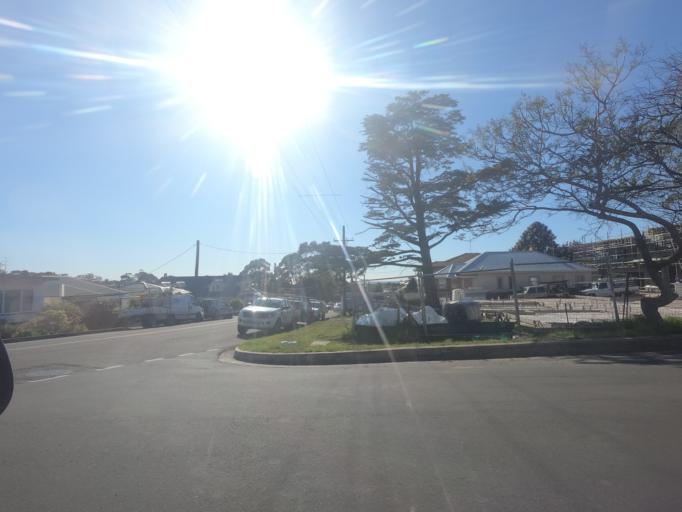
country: AU
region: New South Wales
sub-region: Wollongong
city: Corrimal
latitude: -34.3658
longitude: 150.8932
